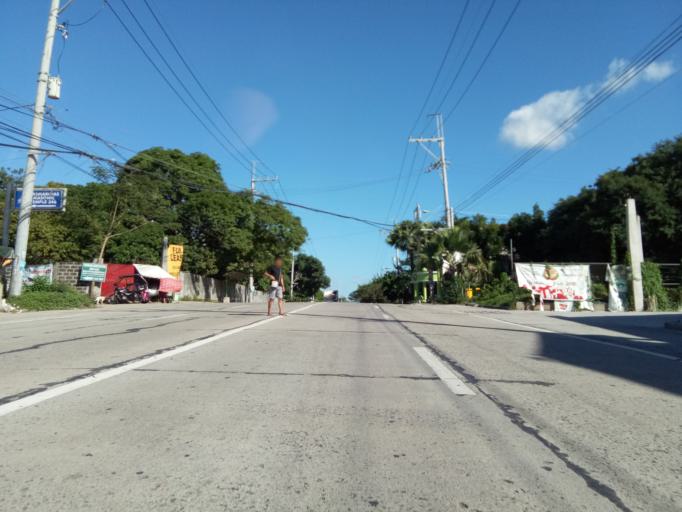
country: PH
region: Calabarzon
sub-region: Province of Cavite
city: Dasmarinas
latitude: 14.3519
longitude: 120.9514
